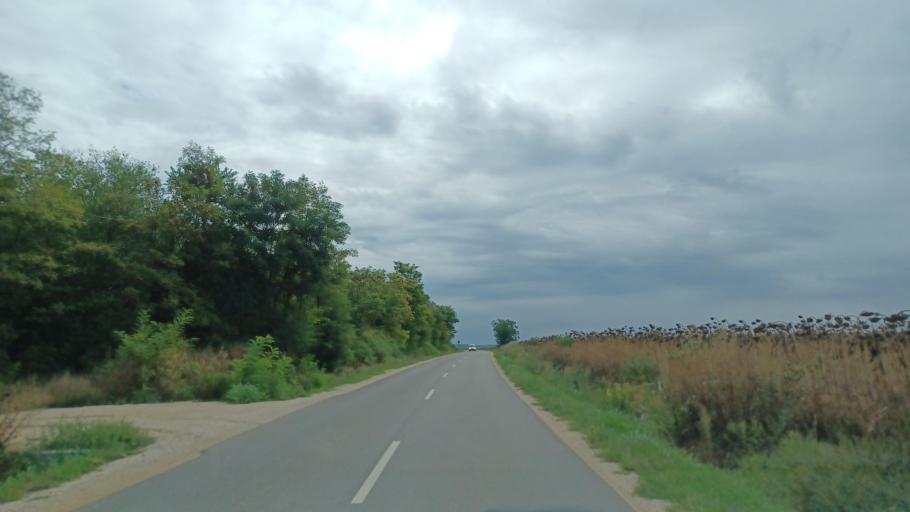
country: HU
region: Tolna
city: Szentgalpuszta
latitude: 46.4124
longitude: 18.6131
